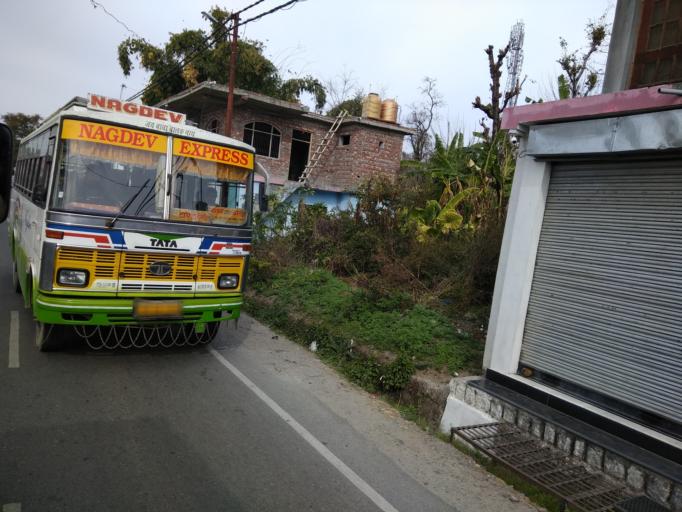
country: IN
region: Himachal Pradesh
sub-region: Kangra
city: Dharmsala
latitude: 32.1882
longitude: 76.3600
